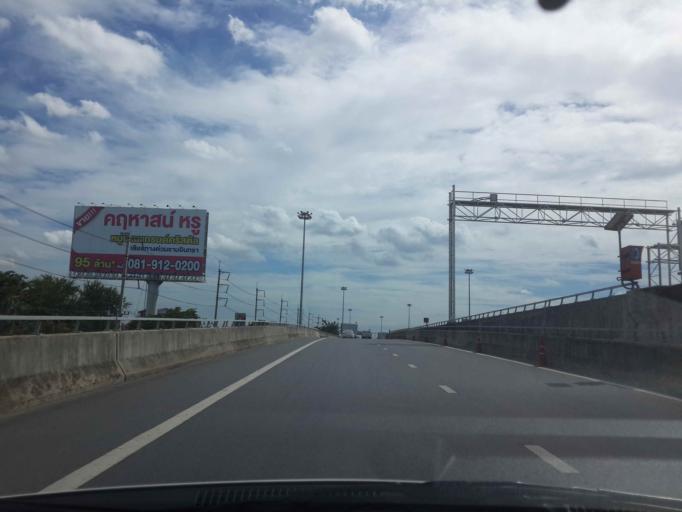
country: TH
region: Bangkok
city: Bang Khen
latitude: 13.8373
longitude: 100.6331
